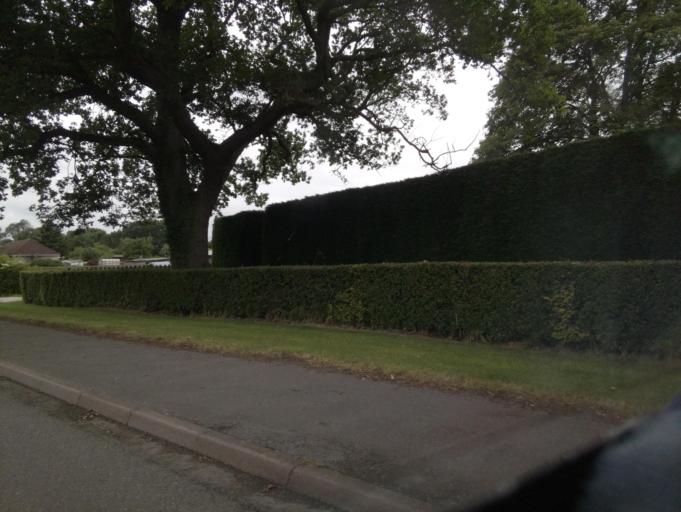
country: GB
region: England
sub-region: Staffordshire
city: Burton upon Trent
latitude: 52.8401
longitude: -1.6672
